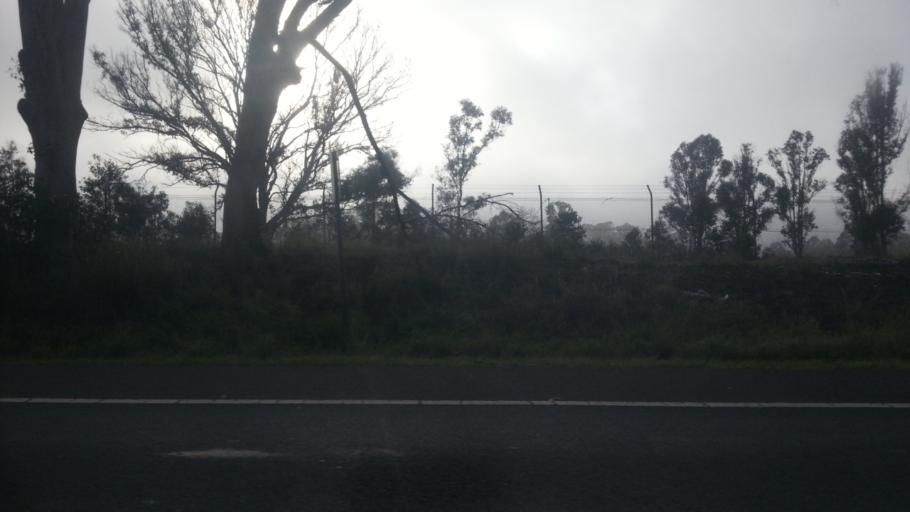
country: AU
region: New South Wales
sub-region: Penrith Municipality
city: Glenmore Park
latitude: -33.8231
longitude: 150.6846
